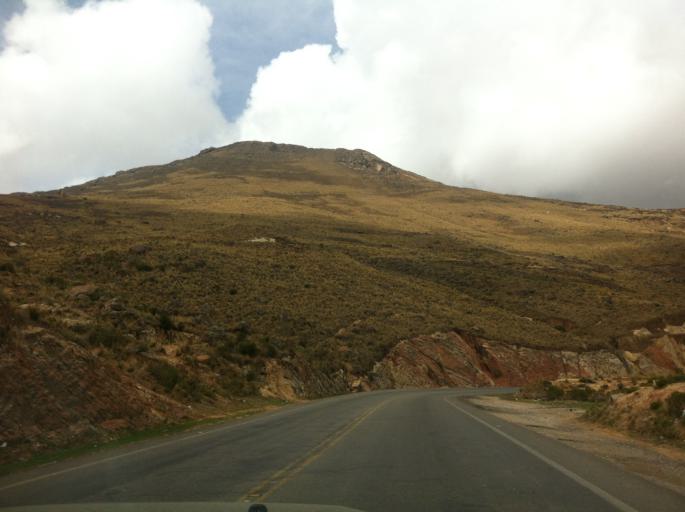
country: BO
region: Cochabamba
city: Irpa Irpa
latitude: -17.7010
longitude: -66.4815
